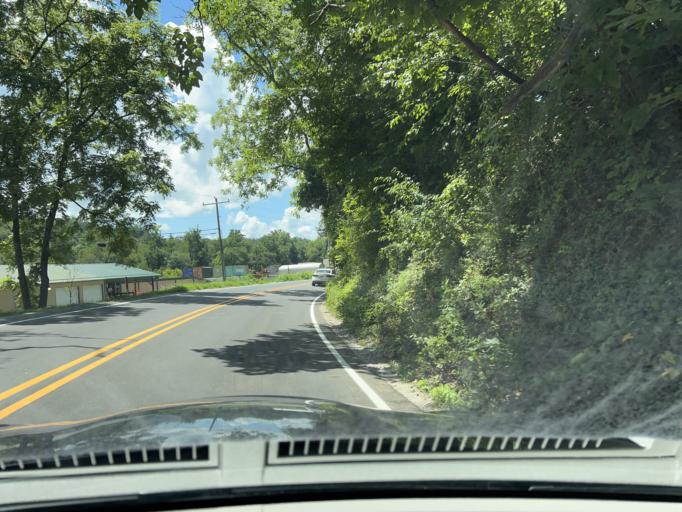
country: US
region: North Carolina
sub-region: Buncombe County
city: Fairview
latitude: 35.5119
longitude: -82.4101
